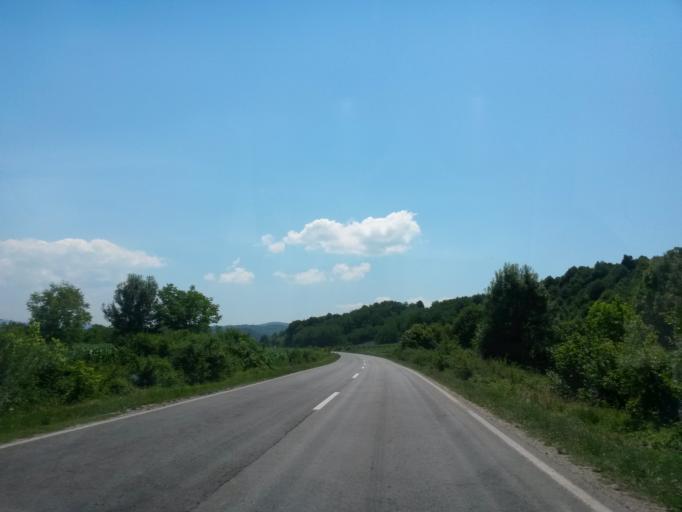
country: BA
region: Republika Srpska
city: Doboj
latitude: 44.8411
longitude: 18.0639
